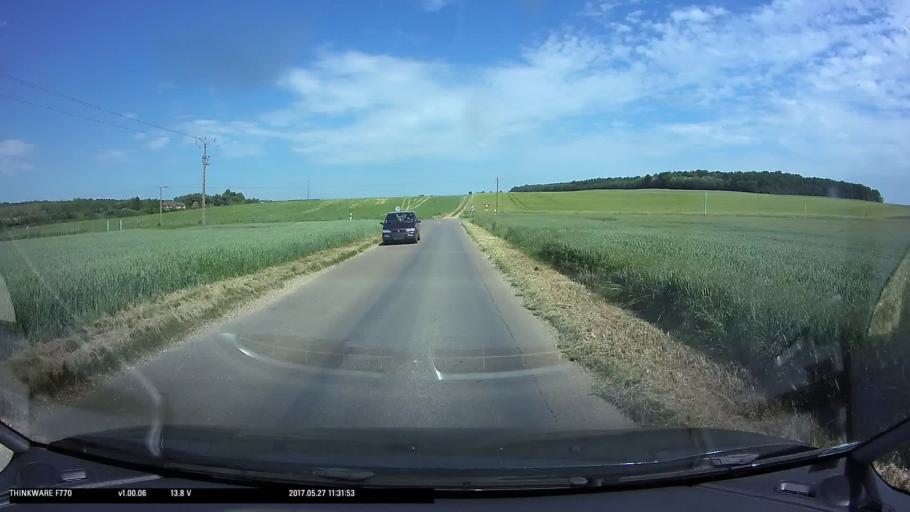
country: FR
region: Haute-Normandie
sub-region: Departement de l'Eure
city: Gisors
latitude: 49.2951
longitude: 1.7832
